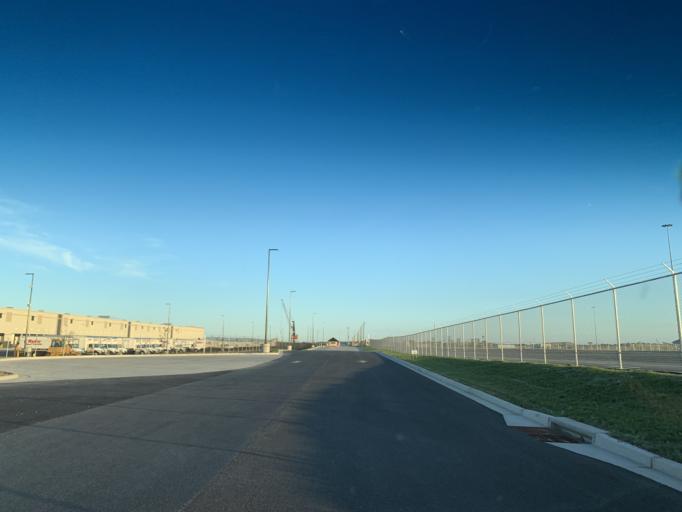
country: US
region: Maryland
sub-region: Baltimore County
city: Edgemere
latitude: 39.2192
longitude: -76.4852
